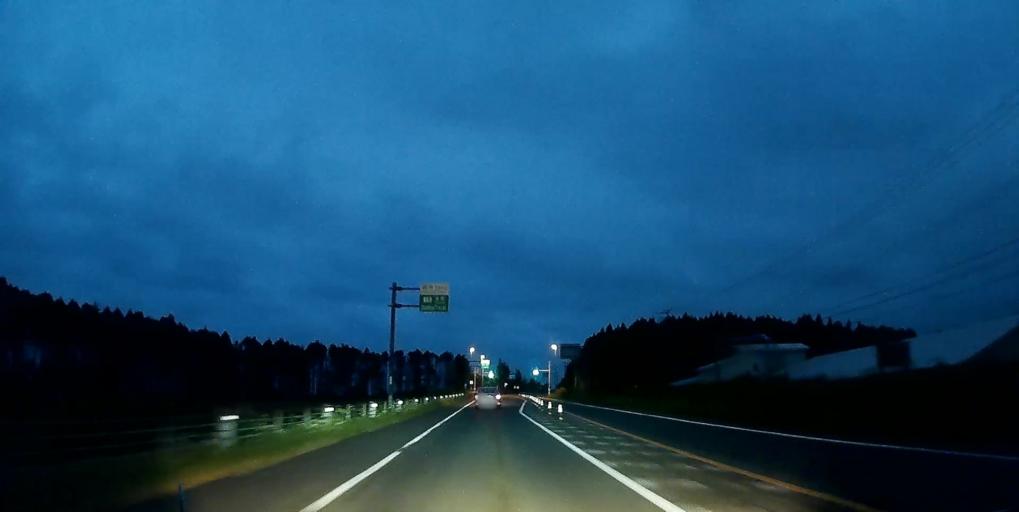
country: JP
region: Hokkaido
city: Nanae
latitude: 42.2086
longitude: 140.3990
